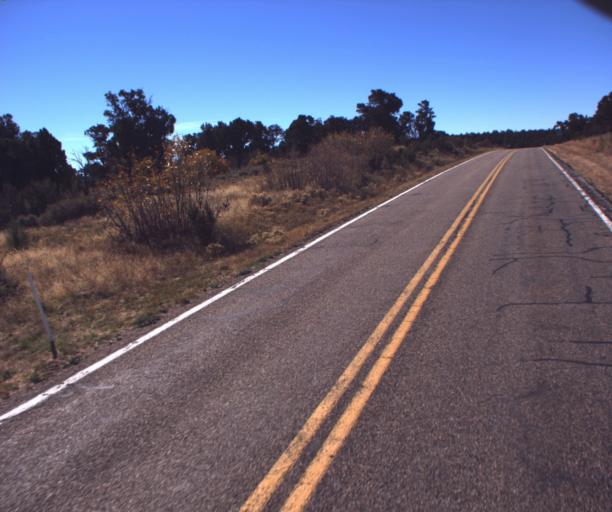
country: US
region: Arizona
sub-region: Coconino County
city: Fredonia
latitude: 36.8130
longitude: -112.2539
